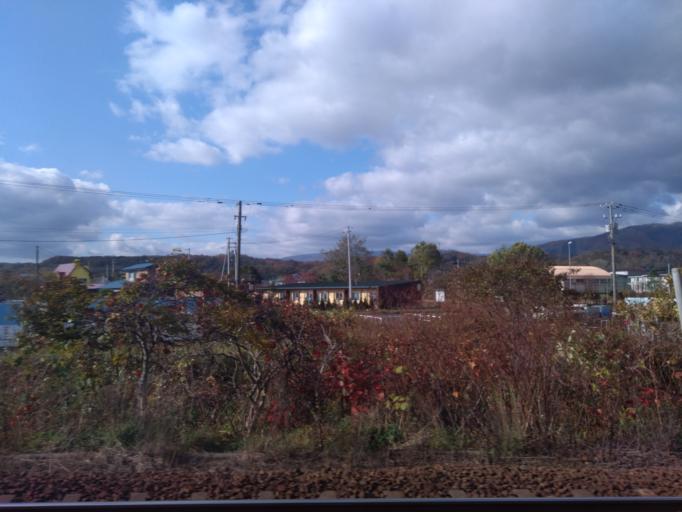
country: JP
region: Hokkaido
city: Shiraoi
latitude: 42.4487
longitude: 141.1750
